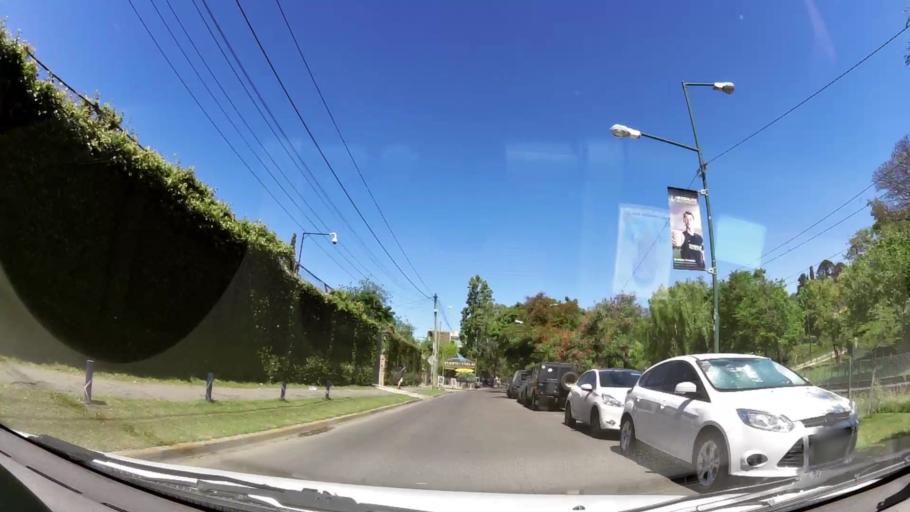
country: AR
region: Buenos Aires
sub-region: Partido de San Isidro
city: San Isidro
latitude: -34.4729
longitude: -58.4915
